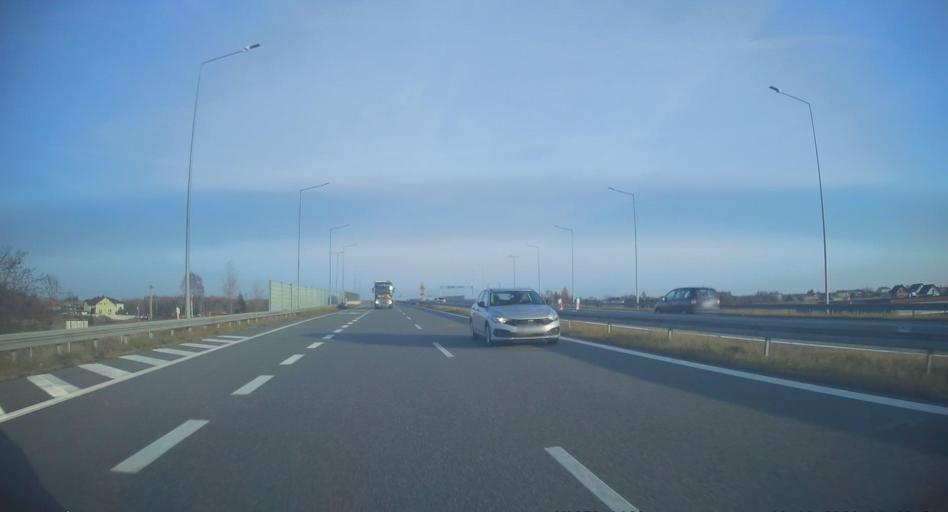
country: PL
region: Silesian Voivodeship
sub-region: Powiat bedzinski
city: Siewierz
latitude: 50.4204
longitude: 19.2003
